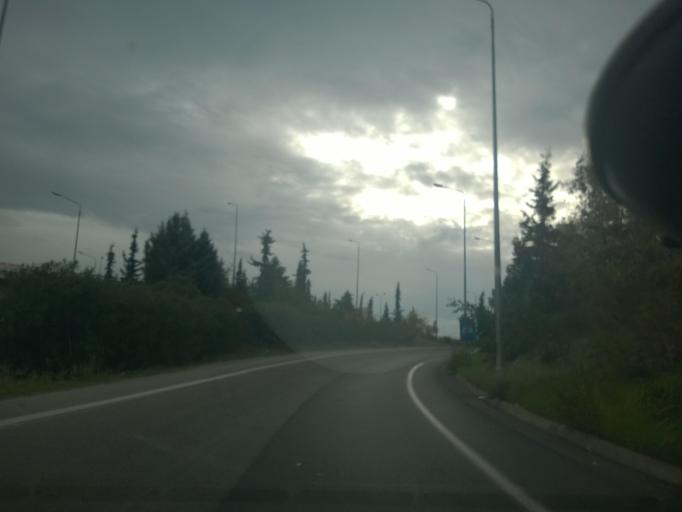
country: GR
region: Central Macedonia
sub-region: Nomos Thessalonikis
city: Pylaia
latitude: 40.5821
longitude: 22.9760
